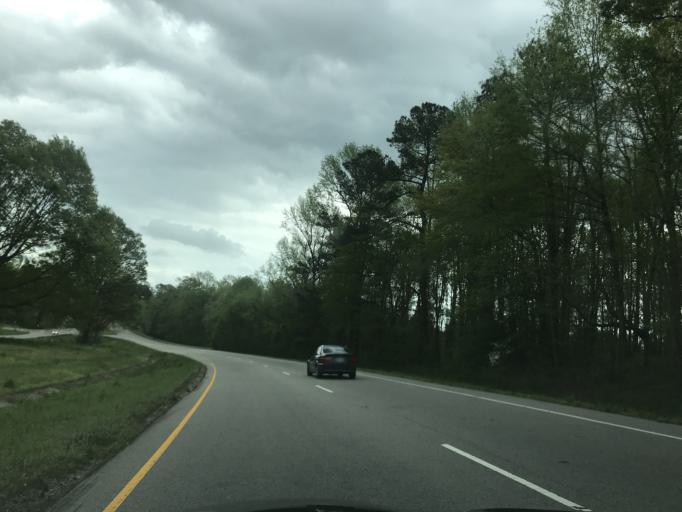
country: US
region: North Carolina
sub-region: Wake County
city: Knightdale
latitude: 35.8039
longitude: -78.4448
